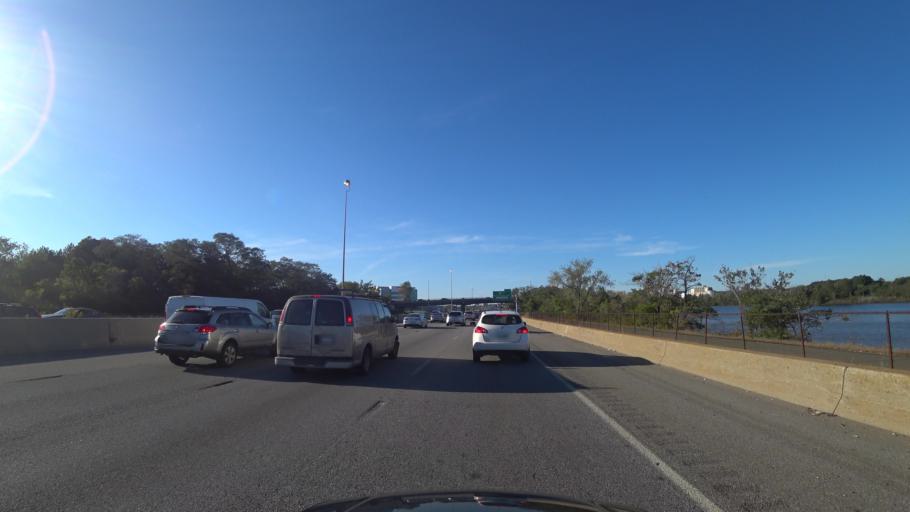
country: US
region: Massachusetts
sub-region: Middlesex County
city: Somerville
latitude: 42.4000
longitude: -71.0938
